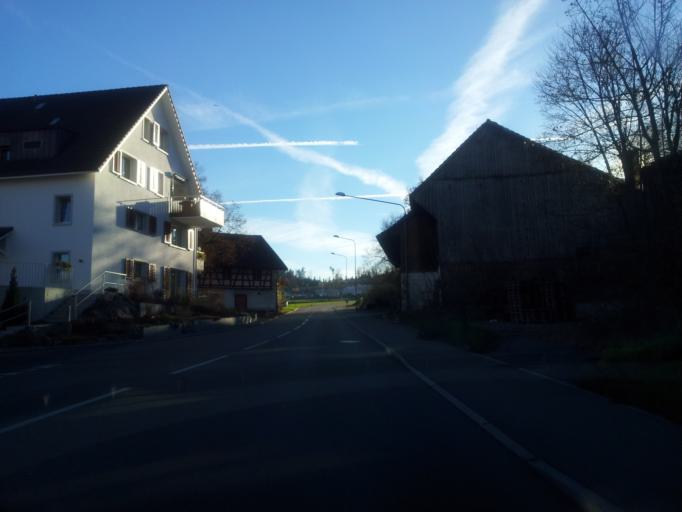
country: CH
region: Zurich
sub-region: Bezirk Dielsdorf
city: Hofstetten
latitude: 47.4641
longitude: 8.4968
